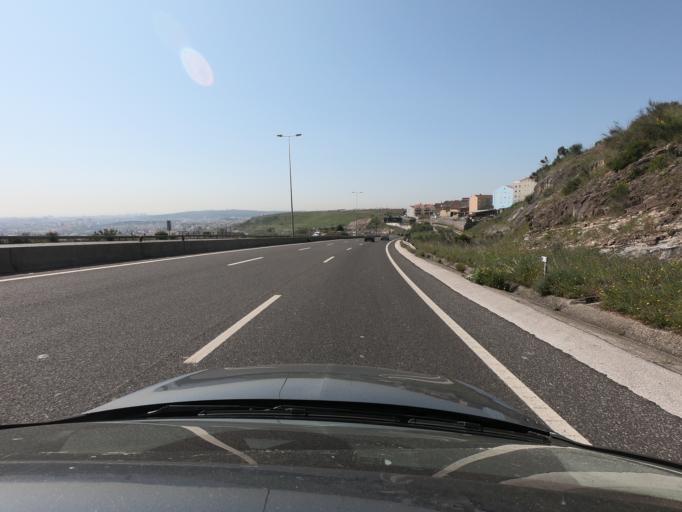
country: PT
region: Lisbon
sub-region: Odivelas
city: Famoes
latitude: 38.7827
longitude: -9.2293
